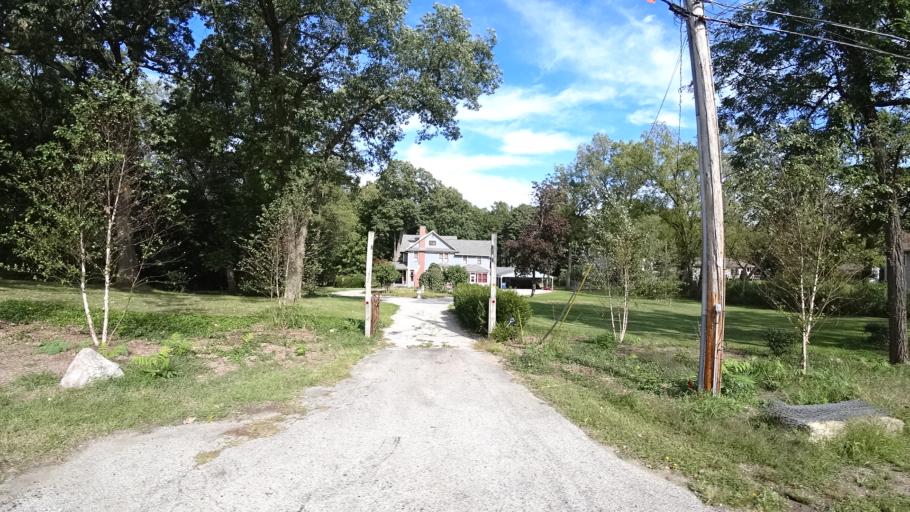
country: US
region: Indiana
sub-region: LaPorte County
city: Michigan City
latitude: 41.7189
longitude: -86.8756
